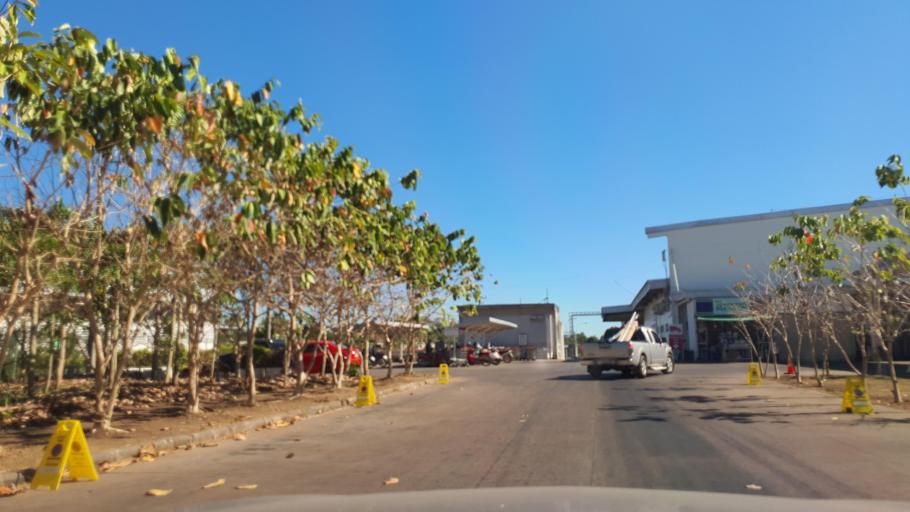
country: TH
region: Nakhon Phanom
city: Nakhon Phanom
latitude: 17.3889
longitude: 104.7672
